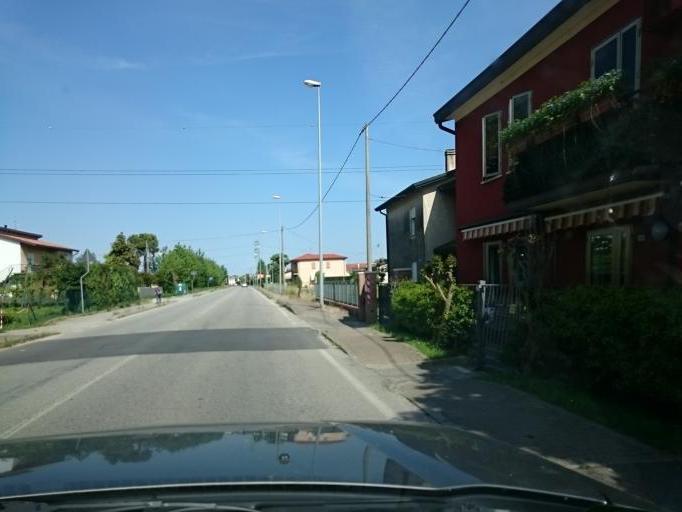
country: IT
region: Veneto
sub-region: Provincia di Venezia
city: Sambruson
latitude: 45.4137
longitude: 12.1072
